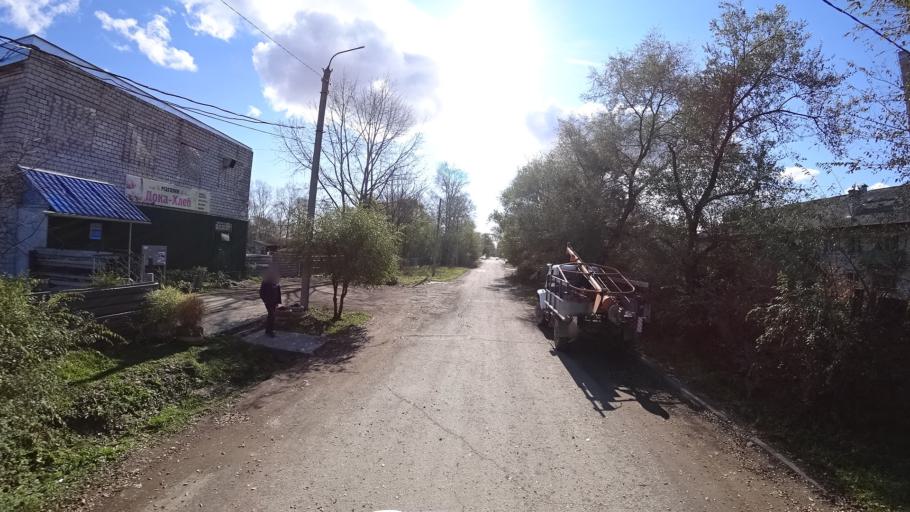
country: RU
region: Khabarovsk Krai
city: Amursk
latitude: 50.1007
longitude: 136.4969
